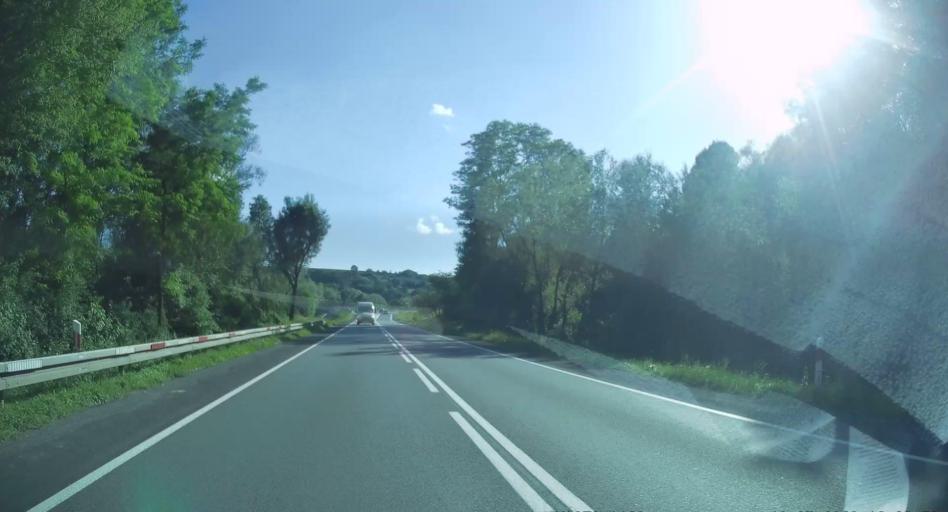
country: PL
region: Lesser Poland Voivodeship
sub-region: Powiat nowosadecki
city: Lososina Dolna
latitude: 49.7673
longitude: 20.6351
